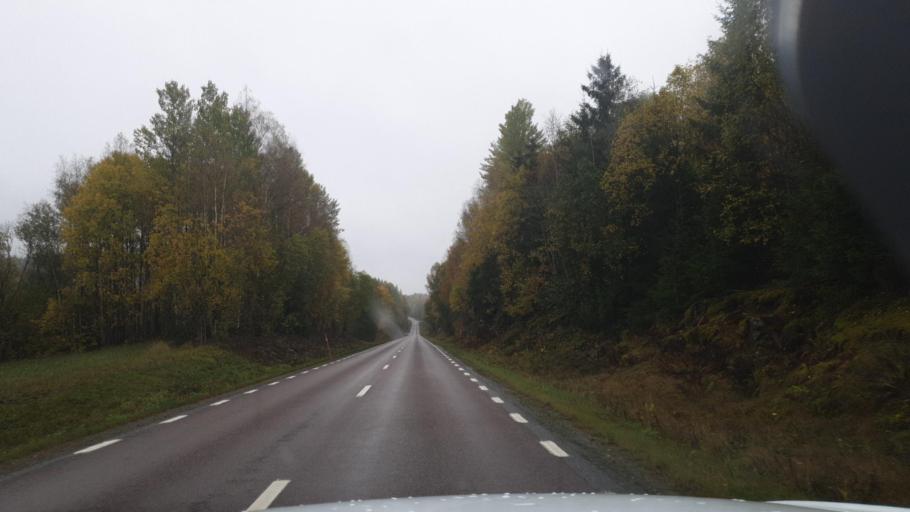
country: SE
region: Vaermland
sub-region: Eda Kommun
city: Amotfors
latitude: 59.7088
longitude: 12.2974
